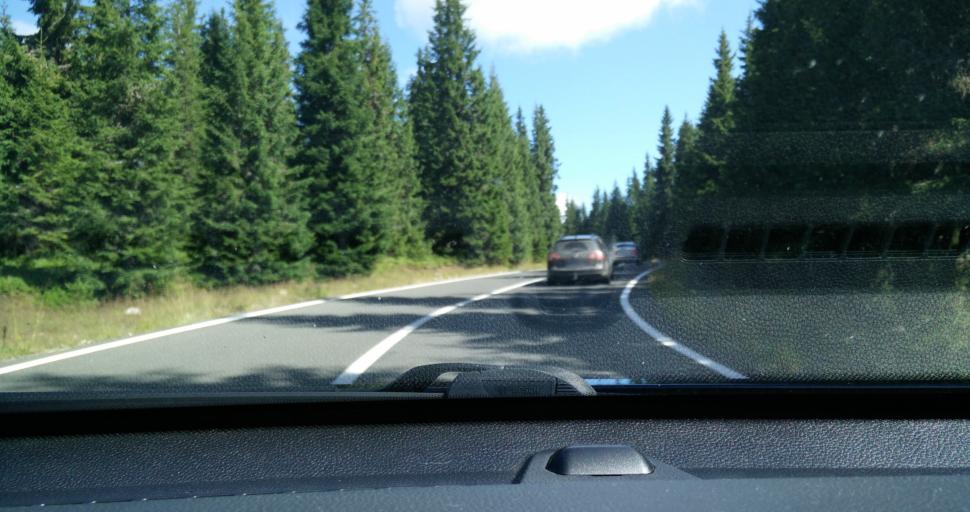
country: RO
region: Hunedoara
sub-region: Oras Petrila
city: Petrila
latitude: 45.4689
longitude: 23.6329
